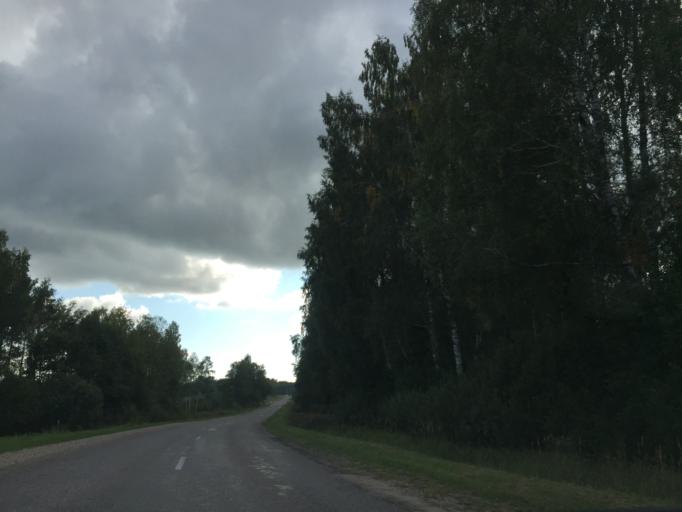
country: LV
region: Limbazu Rajons
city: Limbazi
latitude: 57.3717
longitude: 24.6832
